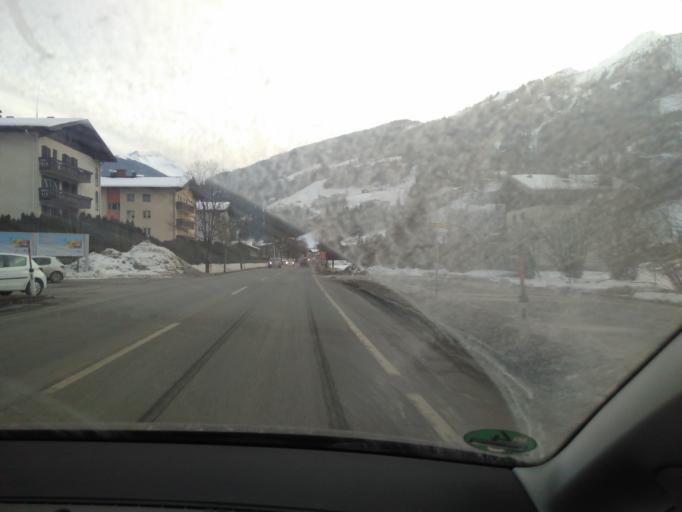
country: AT
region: Salzburg
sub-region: Politischer Bezirk Sankt Johann im Pongau
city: Bad Hofgastein
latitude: 47.1770
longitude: 13.1008
